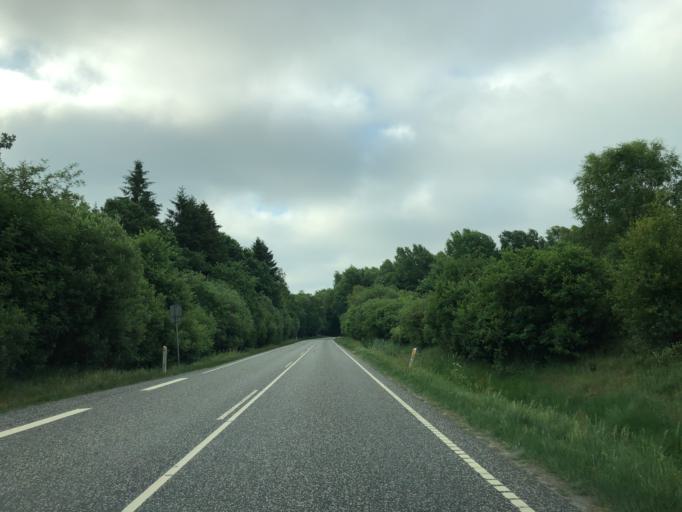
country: DK
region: South Denmark
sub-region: Vejle Kommune
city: Give
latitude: 55.7956
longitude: 9.2700
